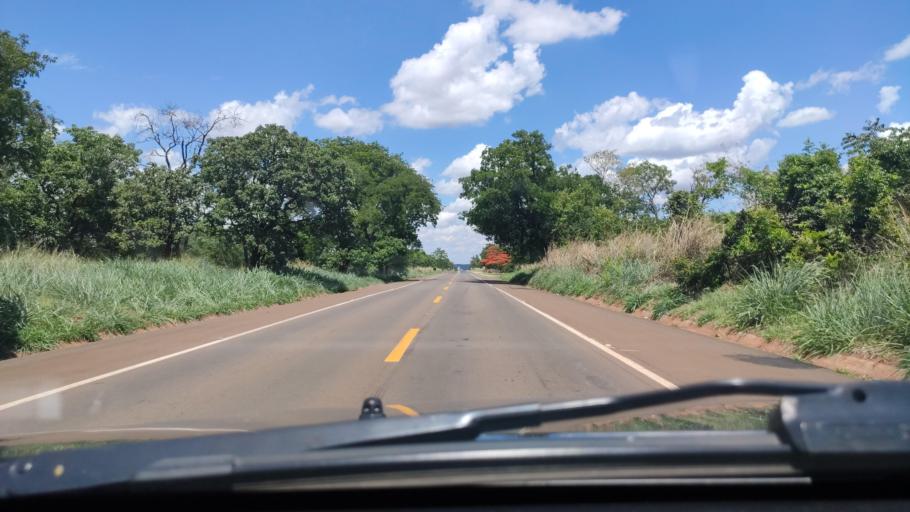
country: BR
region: Sao Paulo
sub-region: Boa Esperanca Do Sul
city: Boa Esperanca do Sul
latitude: -22.0694
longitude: -48.4009
